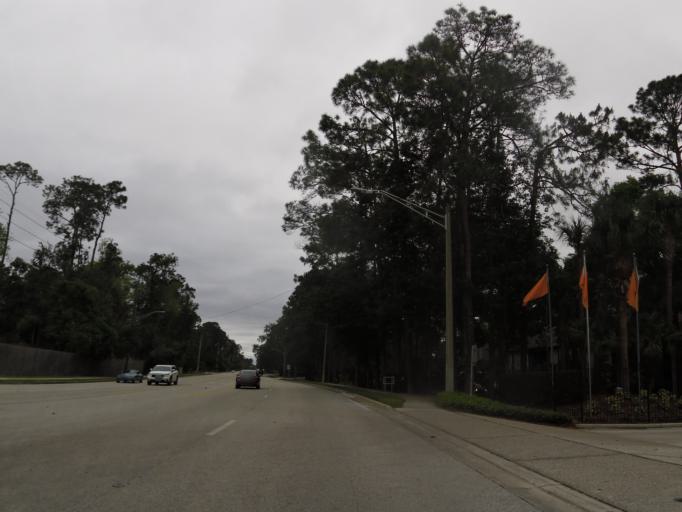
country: US
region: Florida
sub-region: Saint Johns County
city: Fruit Cove
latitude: 30.1906
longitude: -81.6082
